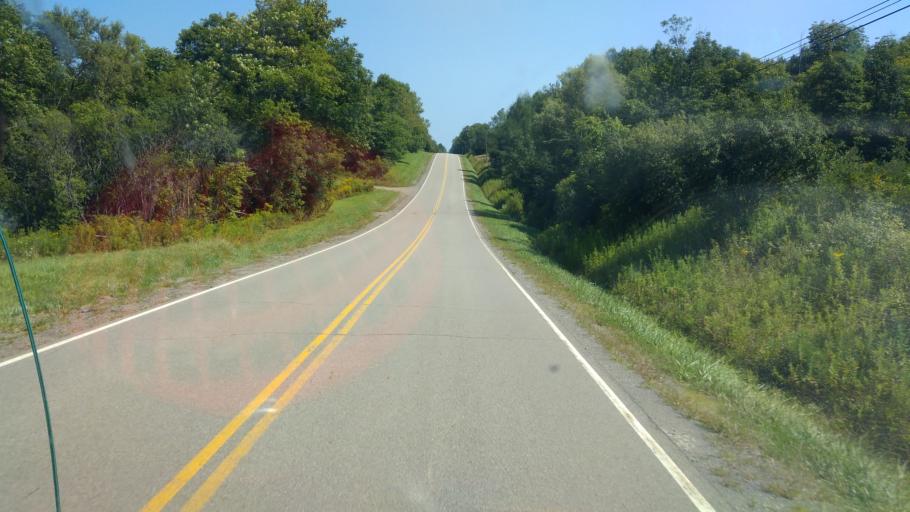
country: US
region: New York
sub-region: Allegany County
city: Belmont
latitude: 42.2920
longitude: -77.9224
